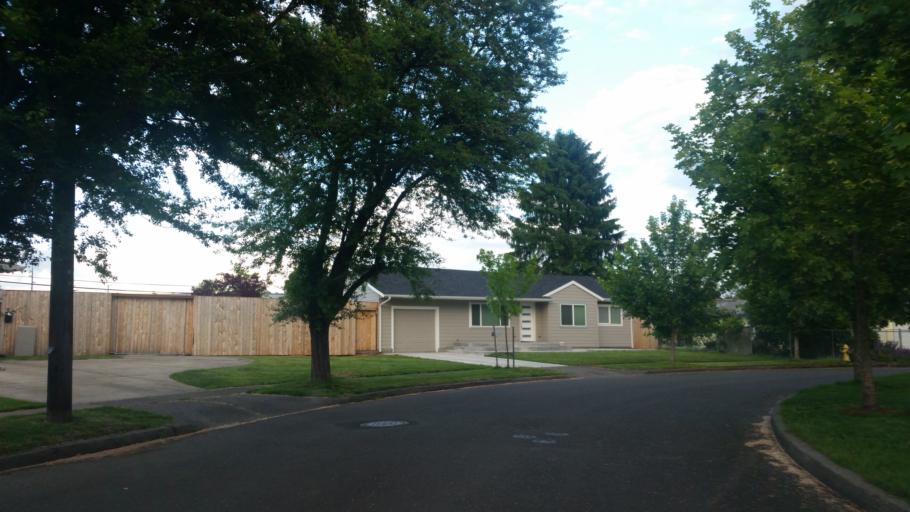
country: US
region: Oregon
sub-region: Washington County
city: Beaverton
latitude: 45.4857
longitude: -122.7895
